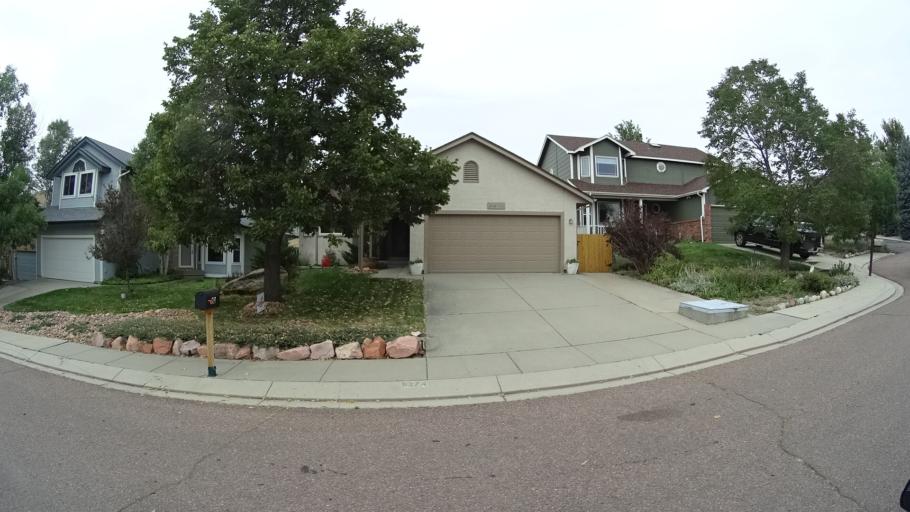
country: US
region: Colorado
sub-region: El Paso County
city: Cimarron Hills
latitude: 38.9088
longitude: -104.7319
